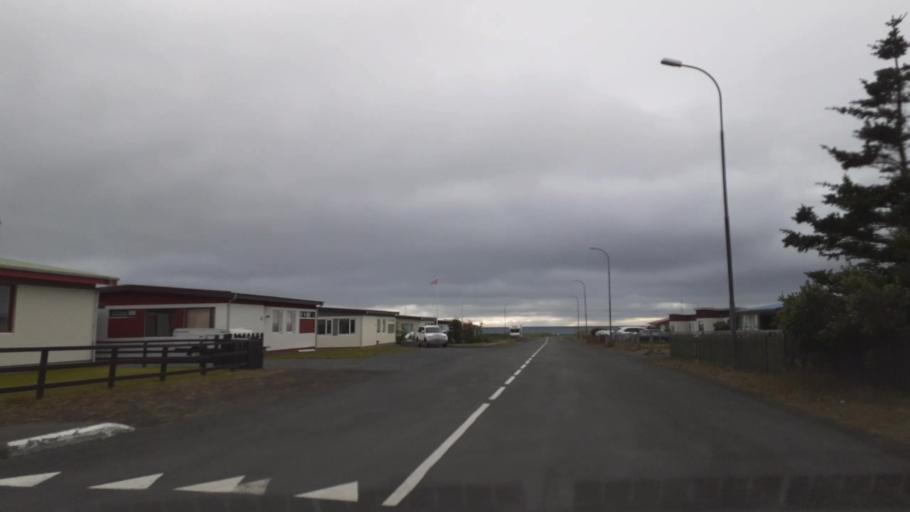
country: IS
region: Northeast
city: Husavik
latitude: 66.3025
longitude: -16.4450
